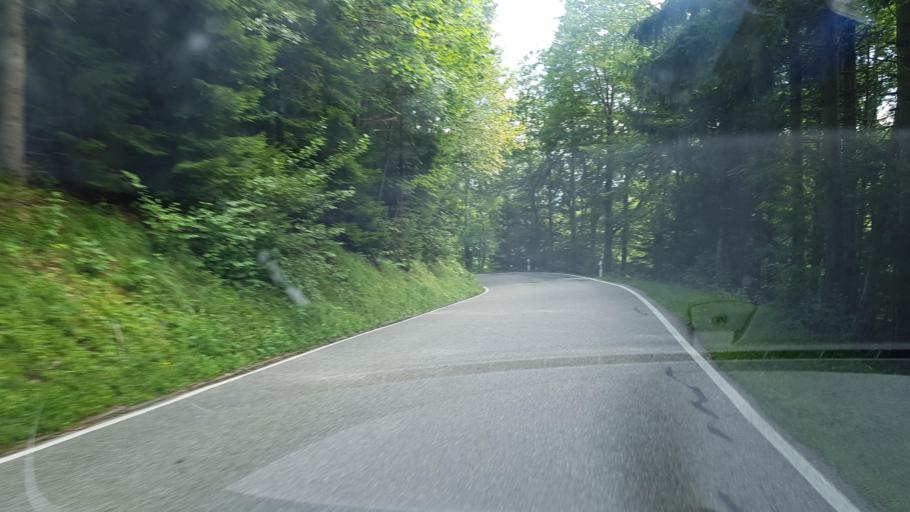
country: CH
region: Solothurn
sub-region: Bezirk Lebern
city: Riedholz
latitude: 47.2625
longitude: 7.5551
